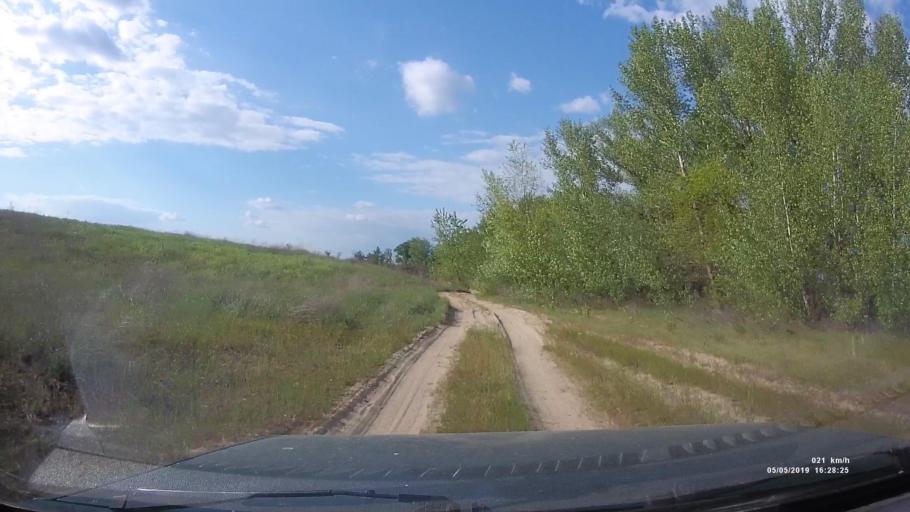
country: RU
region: Rostov
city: Ust'-Donetskiy
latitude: 47.7675
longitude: 41.0159
